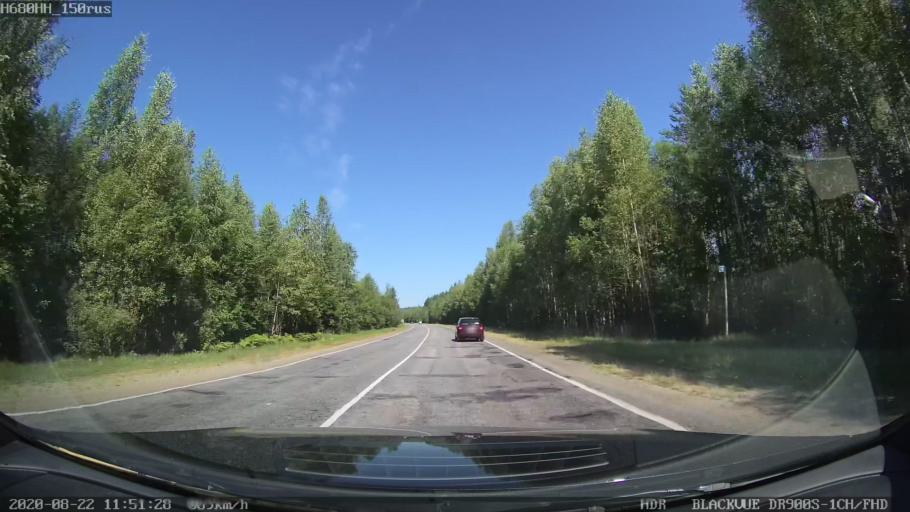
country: RU
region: Tverskaya
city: Sakharovo
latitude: 57.1042
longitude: 36.1205
